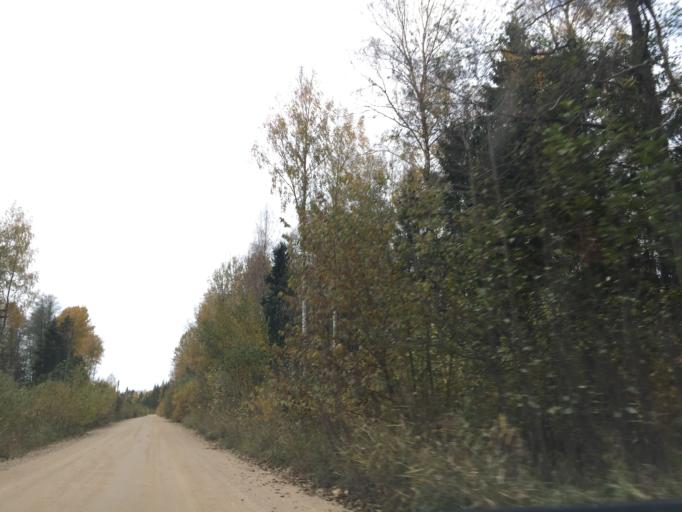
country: LV
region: Salacgrivas
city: Salacgriva
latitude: 57.5677
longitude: 24.4060
